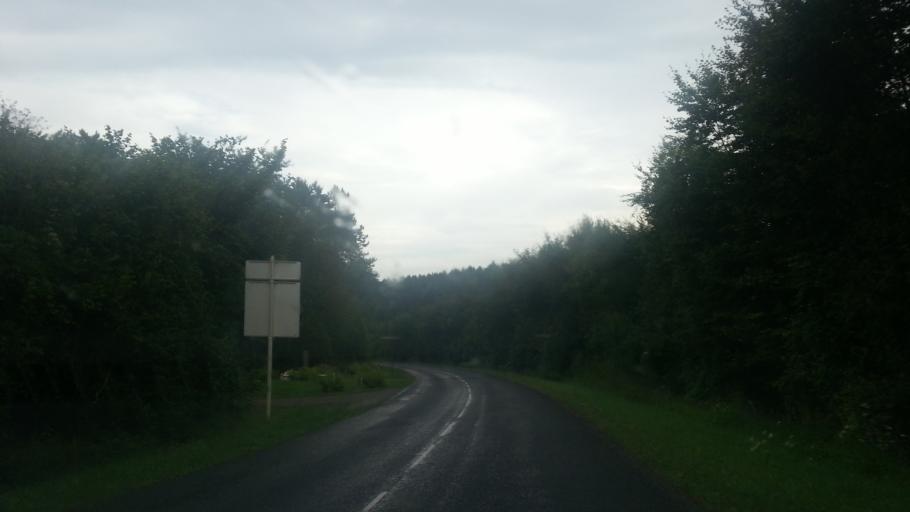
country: FR
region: Lorraine
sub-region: Departement de la Meuse
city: Verdun
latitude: 49.1949
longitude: 5.4445
